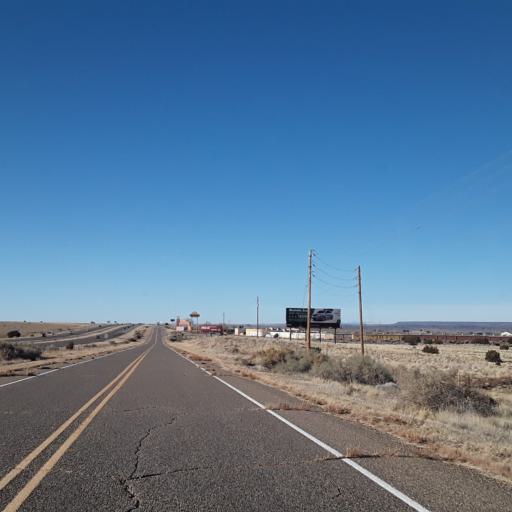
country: US
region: New Mexico
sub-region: Sandoval County
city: Santo Domingo Pueblo
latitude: 35.4566
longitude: -106.3388
